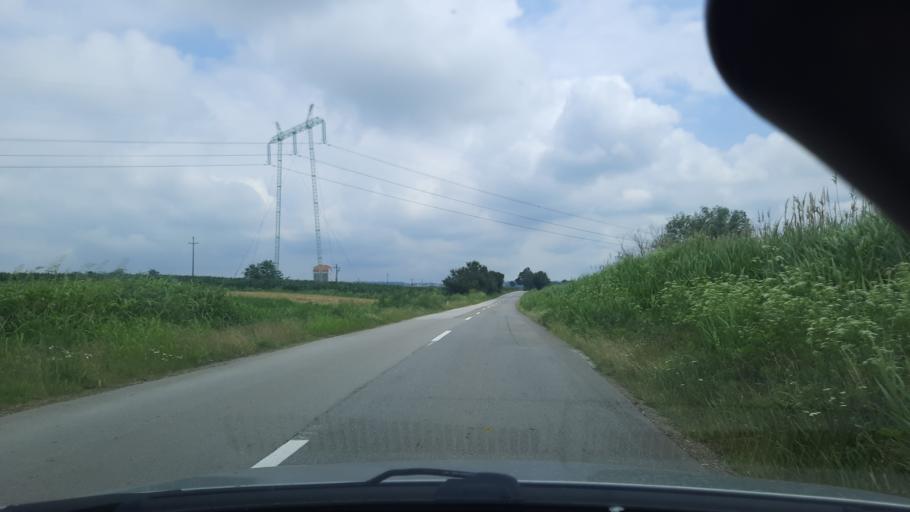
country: RS
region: Central Serbia
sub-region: Branicevski Okrug
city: Malo Crnice
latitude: 44.5789
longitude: 21.3292
